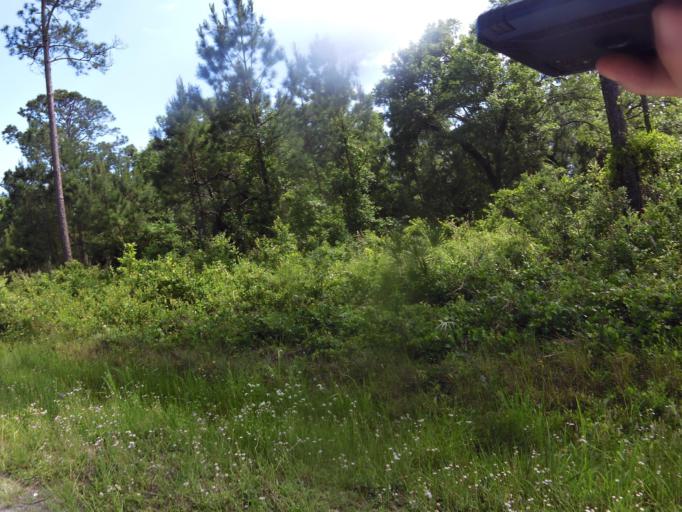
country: US
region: Florida
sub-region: Saint Johns County
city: Palm Valley
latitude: 30.1401
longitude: -81.3722
